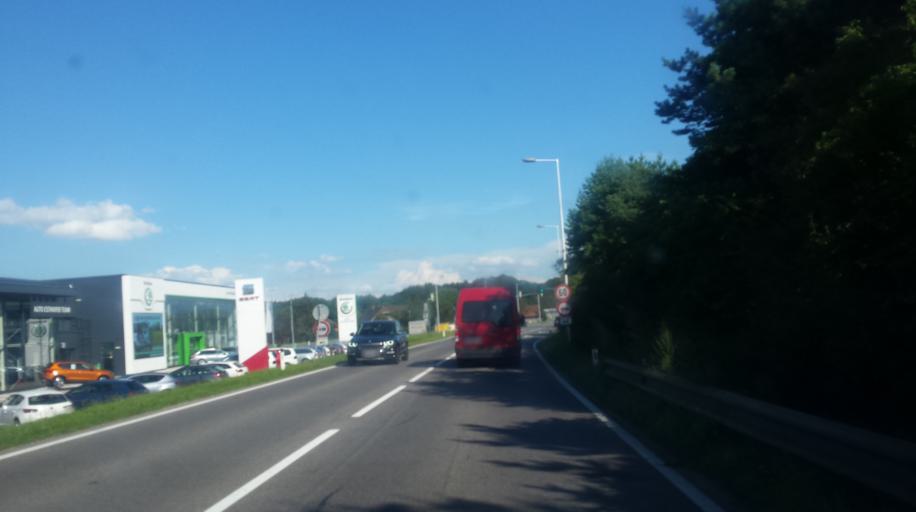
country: AT
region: Upper Austria
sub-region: Politischer Bezirk Vocklabruck
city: Attnang-Puchheim
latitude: 47.9871
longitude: 13.6931
